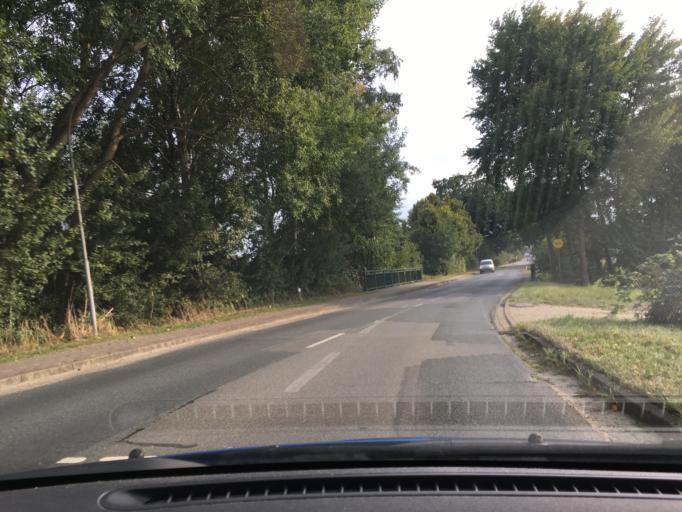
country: DE
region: Lower Saxony
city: Wulfsen
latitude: 53.3052
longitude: 10.1474
